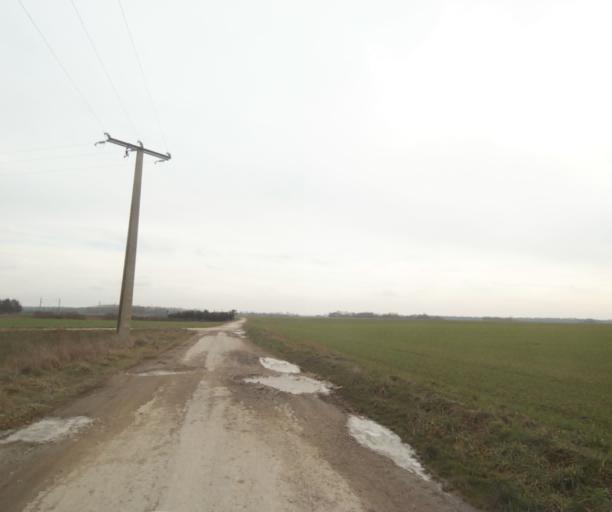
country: FR
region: Champagne-Ardenne
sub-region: Departement de la Haute-Marne
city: Villiers-en-Lieu
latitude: 48.6748
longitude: 4.8718
